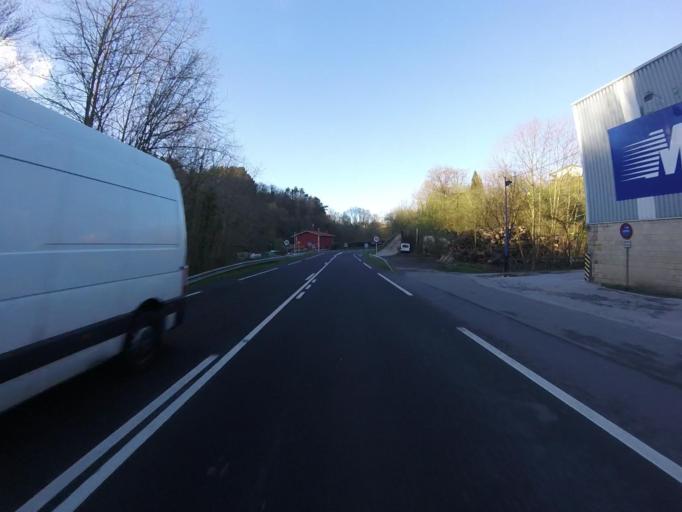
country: ES
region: Basque Country
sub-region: Provincia de Guipuzcoa
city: Errenteria
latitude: 43.2917
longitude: -1.8832
